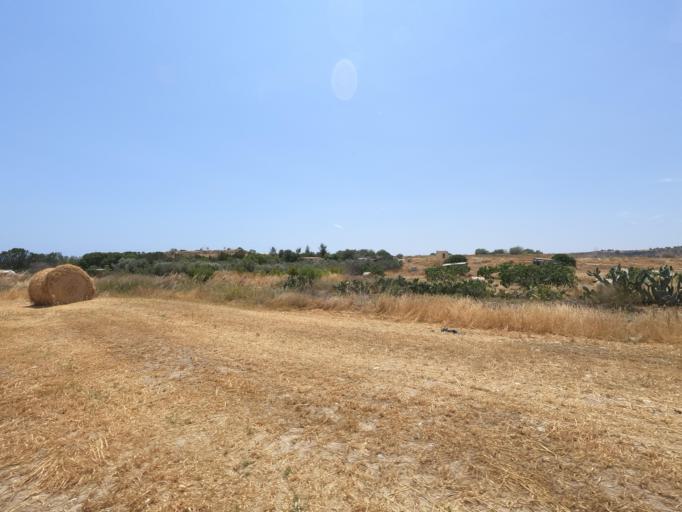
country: CY
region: Larnaka
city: Voroklini
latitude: 34.9925
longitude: 33.6704
